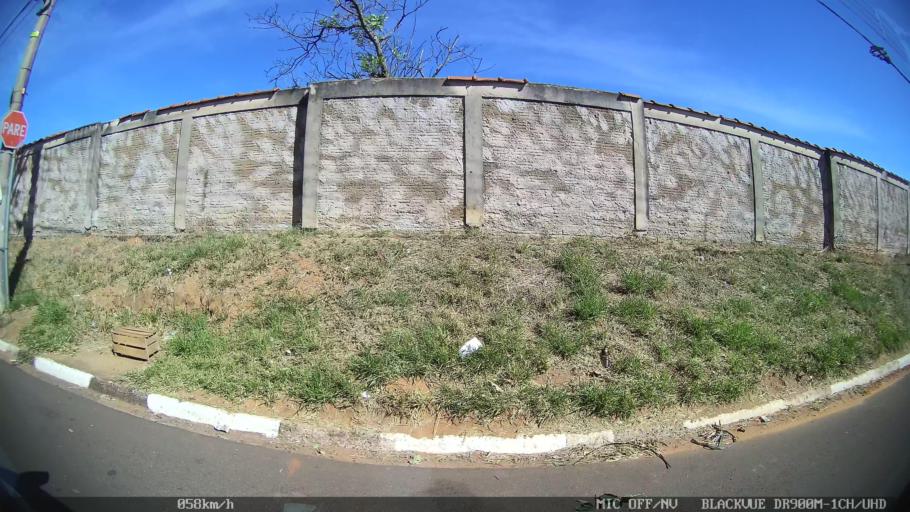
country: BR
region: Sao Paulo
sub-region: Franca
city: Franca
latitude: -20.5640
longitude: -47.3586
